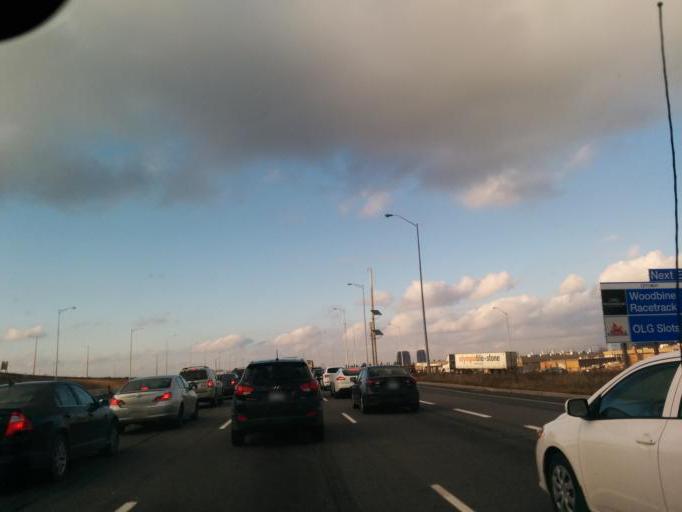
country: CA
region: Ontario
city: Etobicoke
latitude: 43.6981
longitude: -79.6076
